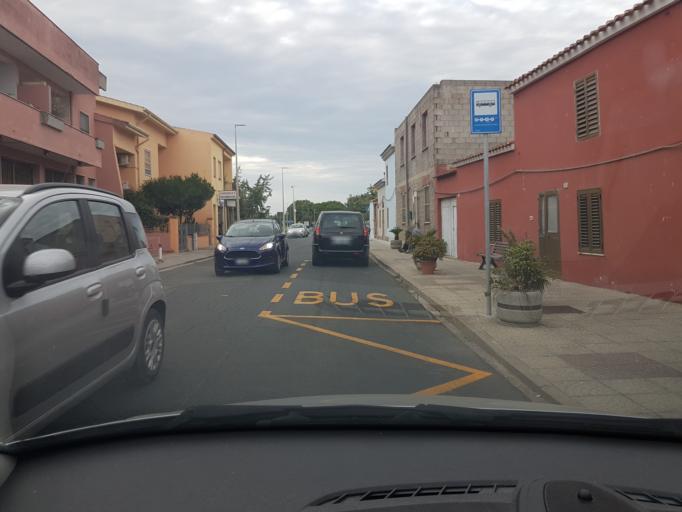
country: IT
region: Sardinia
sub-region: Provincia di Oristano
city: Riola Sardo
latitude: 39.9967
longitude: 8.5388
